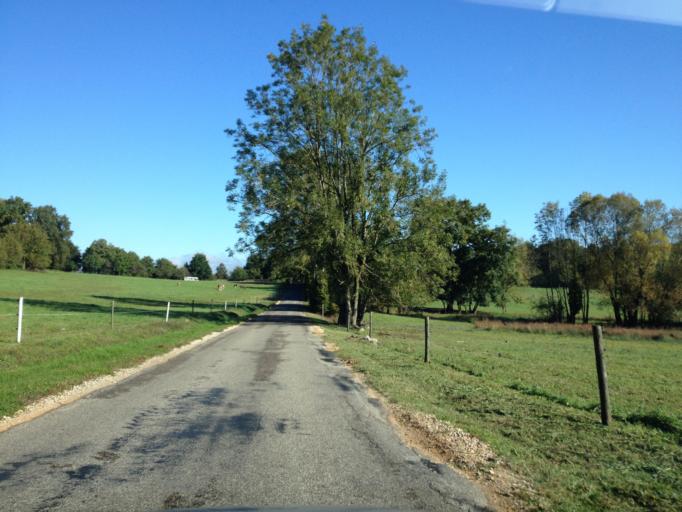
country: FR
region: Rhone-Alpes
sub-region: Departement de l'Isere
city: Morestel
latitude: 45.6672
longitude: 5.4561
